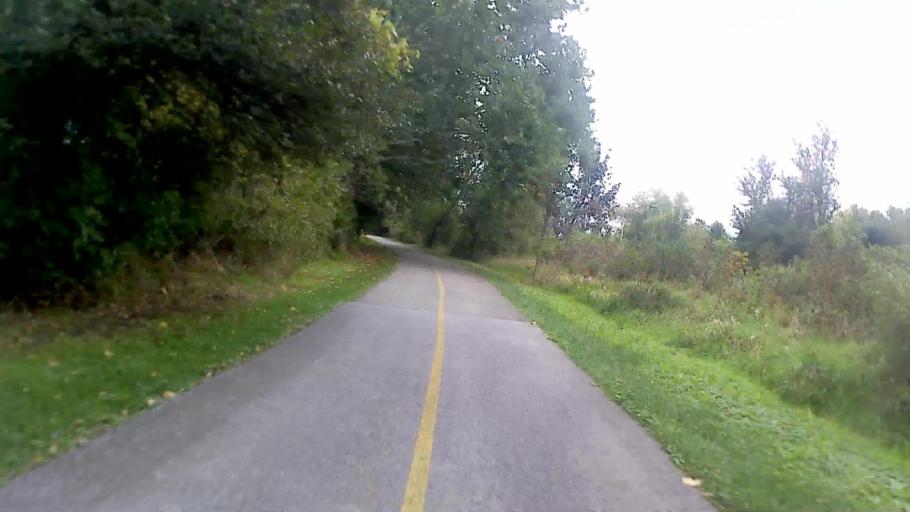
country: US
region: Illinois
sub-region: Kane County
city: Montgomery
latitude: 41.7482
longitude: -88.3652
